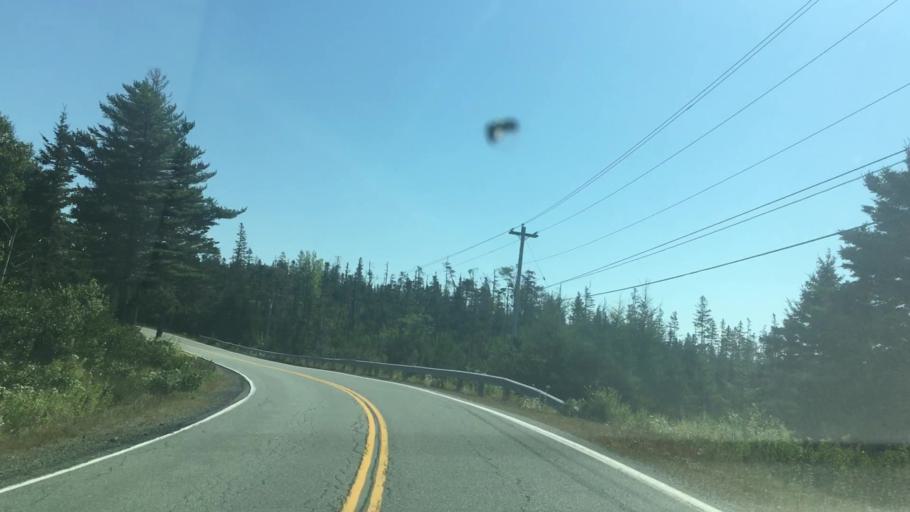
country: CA
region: Nova Scotia
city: Antigonish
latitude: 45.0073
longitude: -62.0893
